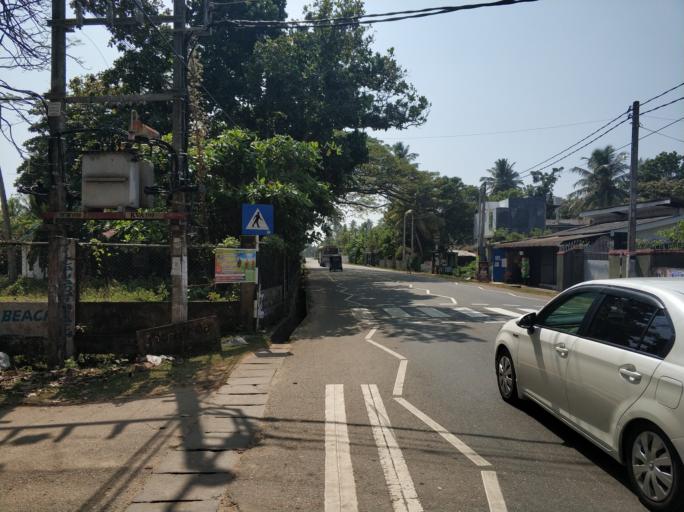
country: LK
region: Southern
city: Weligama
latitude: 5.9624
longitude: 80.4025
